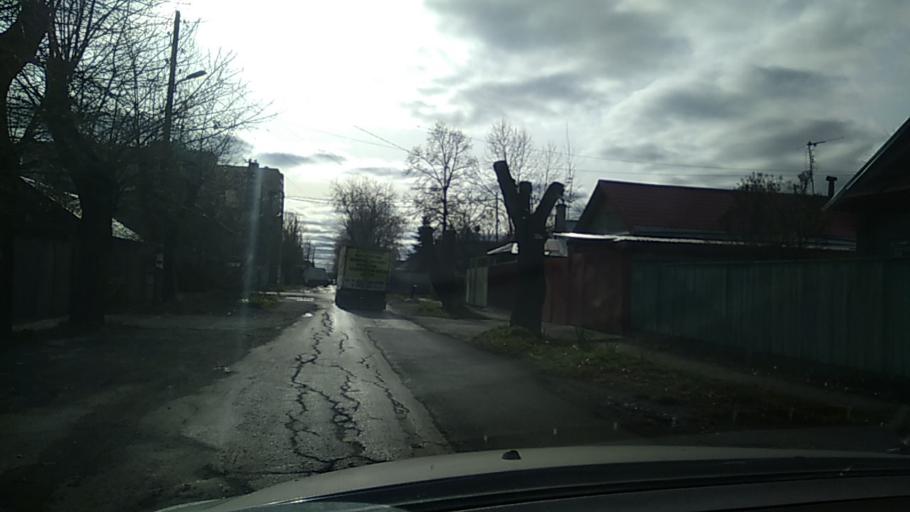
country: RU
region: Sverdlovsk
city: Sovkhoznyy
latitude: 56.7669
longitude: 60.5979
